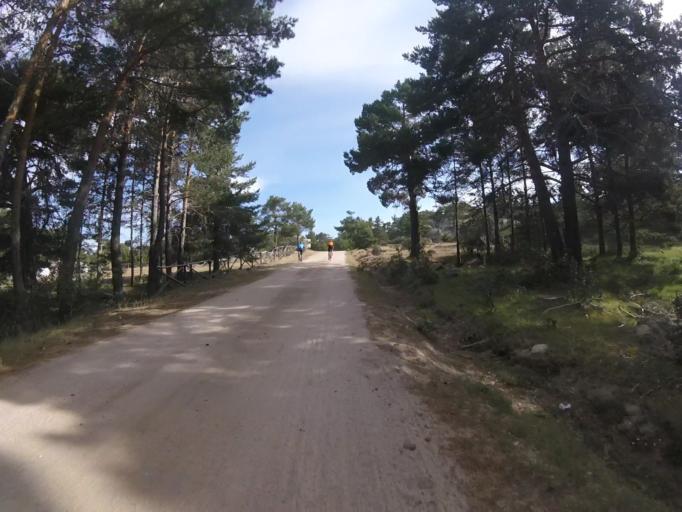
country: ES
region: Castille and Leon
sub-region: Provincia de Avila
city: Peguerinos
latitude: 40.6472
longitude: -4.1781
